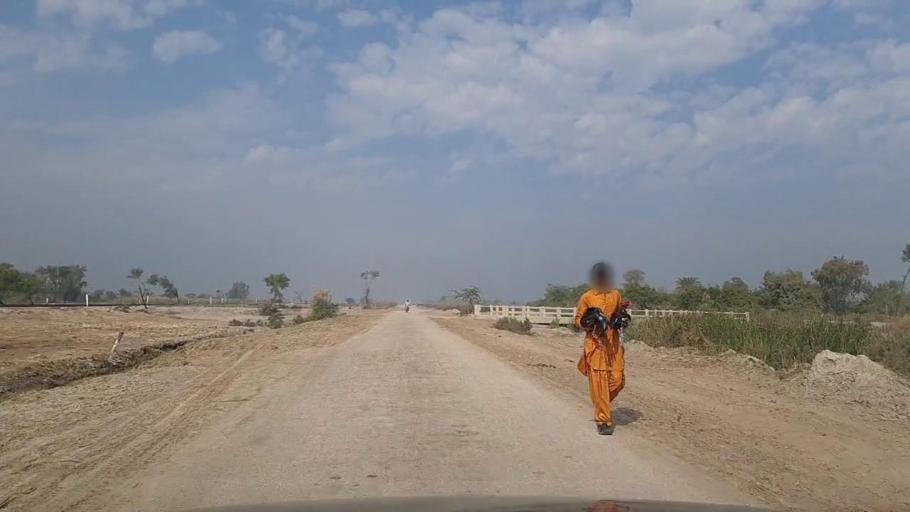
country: PK
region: Sindh
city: Daur
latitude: 26.3825
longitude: 68.3538
